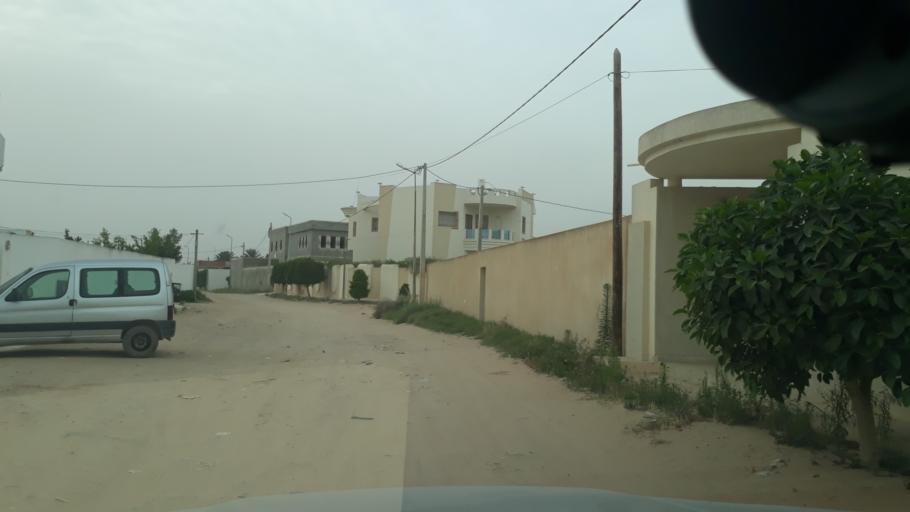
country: TN
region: Safaqis
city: Al Qarmadah
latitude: 34.7819
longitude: 10.7650
